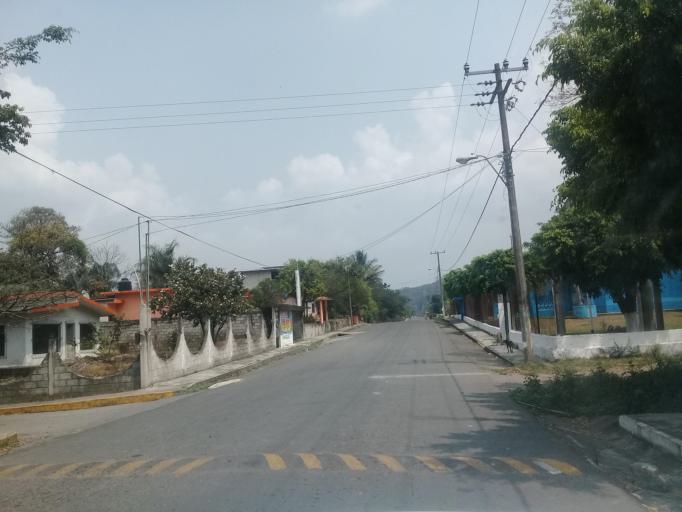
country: MX
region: Veracruz
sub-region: Cordoba
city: San Jose de Tapia
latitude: 18.8175
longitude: -96.9819
